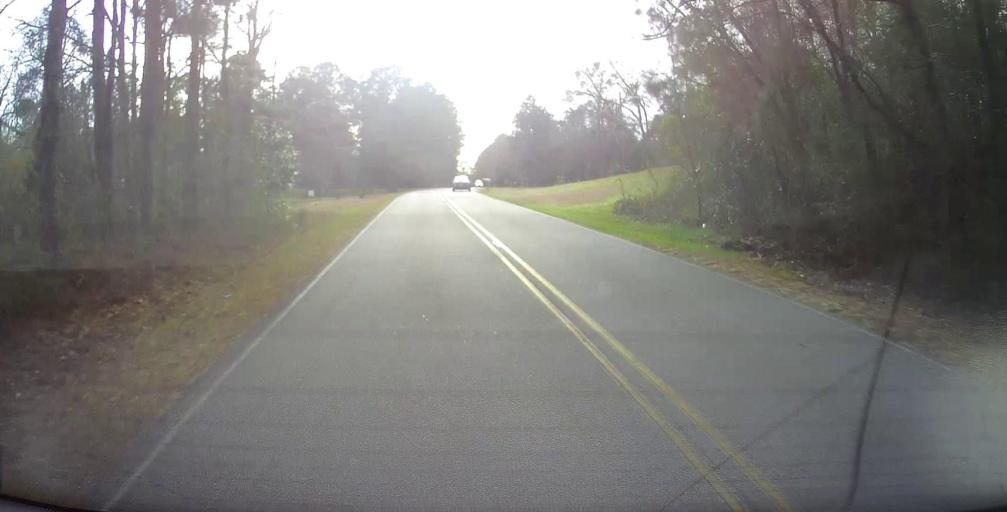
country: US
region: Georgia
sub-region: Harris County
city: Hamilton
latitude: 32.6302
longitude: -84.8057
